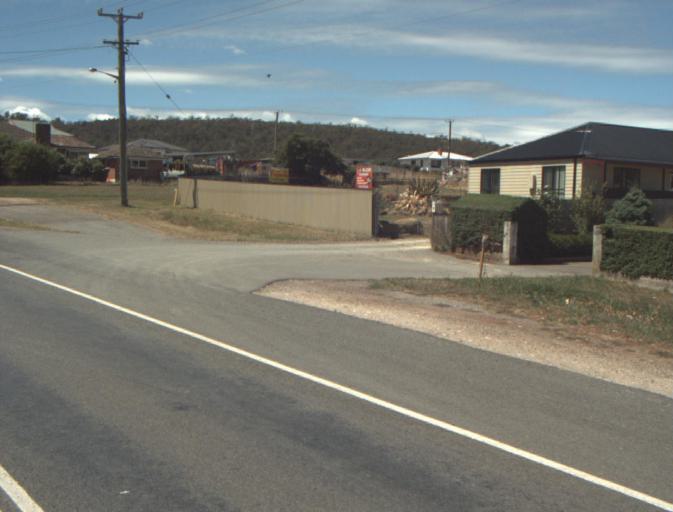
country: AU
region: Tasmania
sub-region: Launceston
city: Mayfield
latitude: -41.3708
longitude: 147.1393
